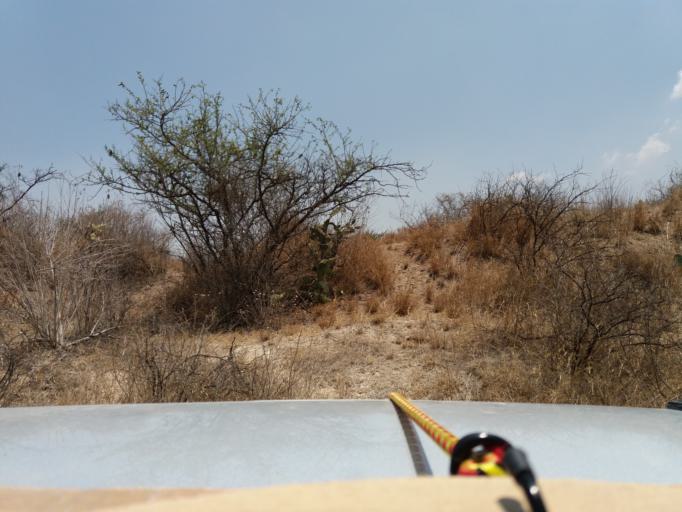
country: MX
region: Aguascalientes
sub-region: Aguascalientes
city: San Sebastian [Fraccionamiento]
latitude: 21.7749
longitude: -102.3301
